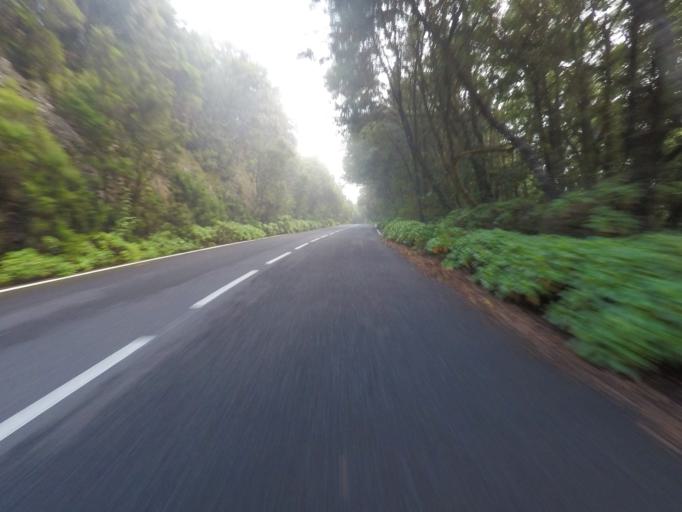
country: ES
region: Canary Islands
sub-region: Provincia de Santa Cruz de Tenerife
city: Hermigua
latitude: 28.1184
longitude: -17.2187
